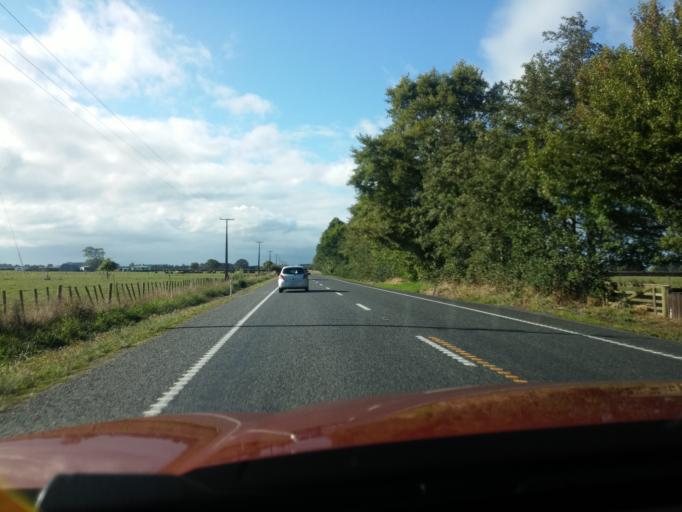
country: NZ
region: Waikato
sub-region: Hauraki District
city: Paeroa
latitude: -37.5649
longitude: 175.5503
